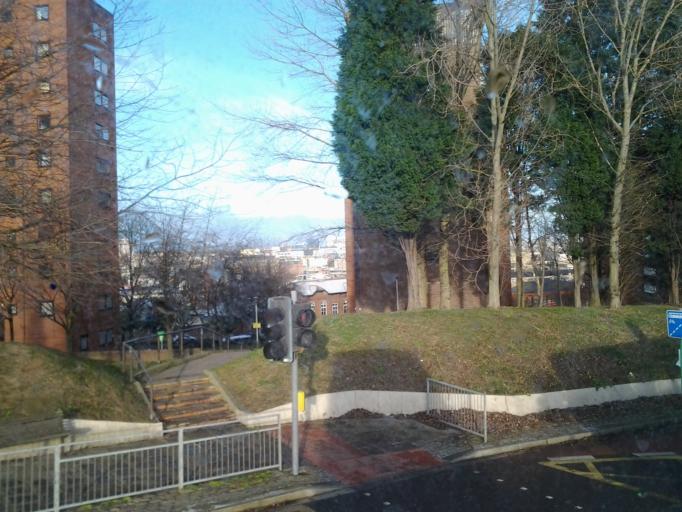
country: GB
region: England
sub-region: Gateshead
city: Gateshead
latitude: 54.9621
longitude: -1.6057
